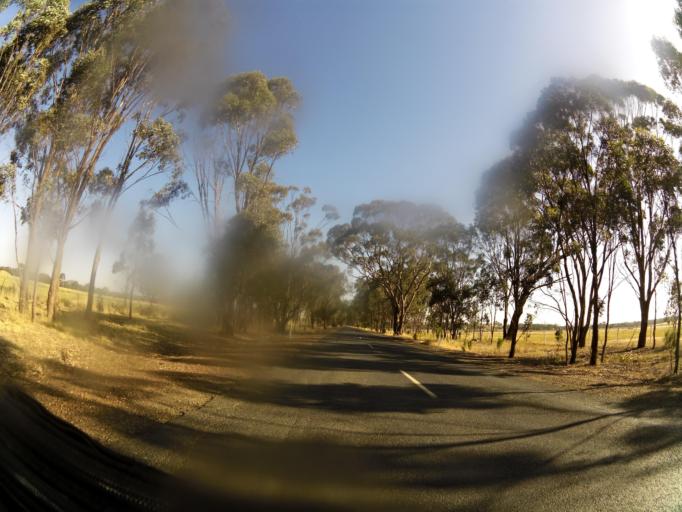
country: AU
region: Victoria
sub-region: Murrindindi
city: Kinglake West
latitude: -36.9760
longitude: 145.1101
